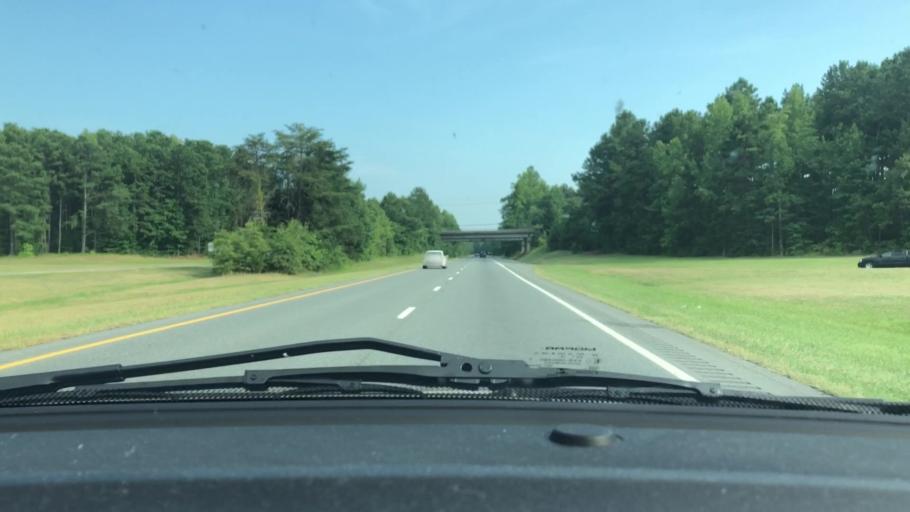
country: US
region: North Carolina
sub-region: Guilford County
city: Forest Oaks
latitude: 35.9163
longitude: -79.6761
